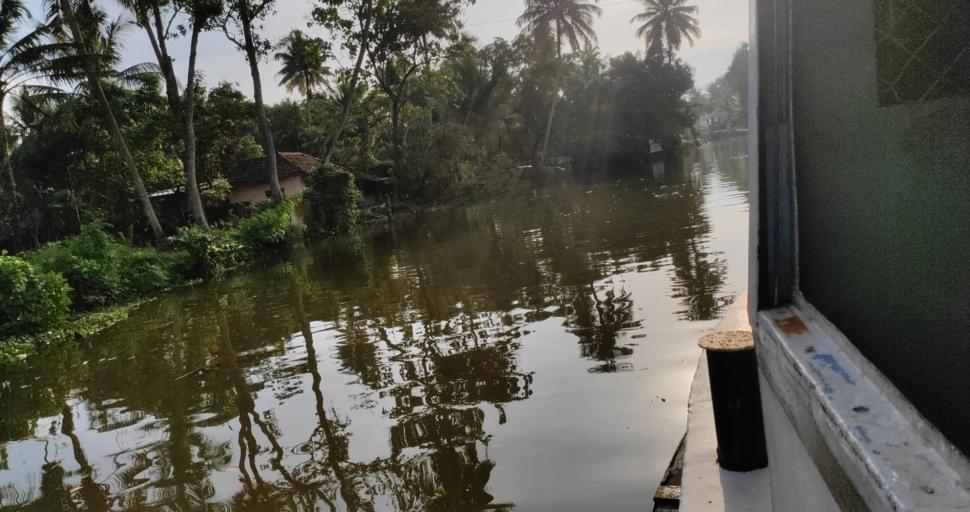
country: IN
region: Kerala
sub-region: Kottayam
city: Kottayam
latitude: 9.5972
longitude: 76.4275
